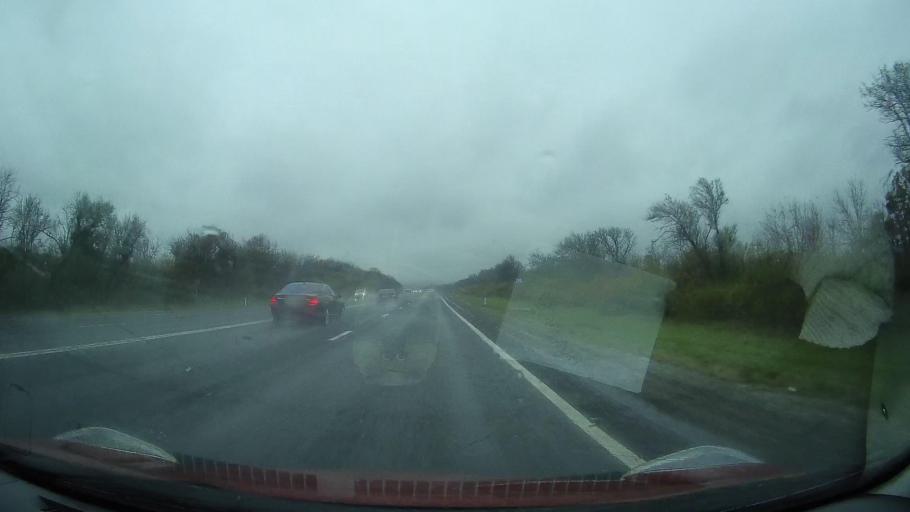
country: RU
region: Stavropol'skiy
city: Nevinnomyssk
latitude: 44.6181
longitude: 42.0987
